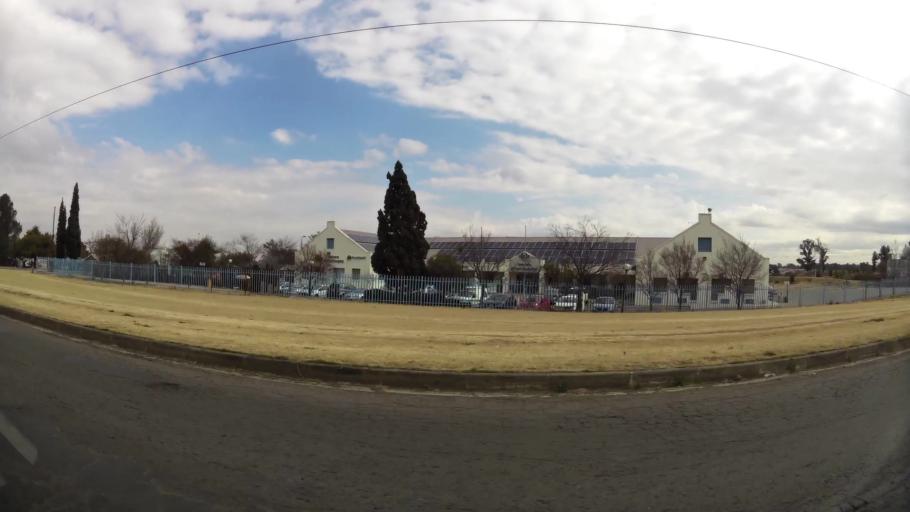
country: ZA
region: Orange Free State
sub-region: Fezile Dabi District Municipality
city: Kroonstad
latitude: -27.6533
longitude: 27.2310
